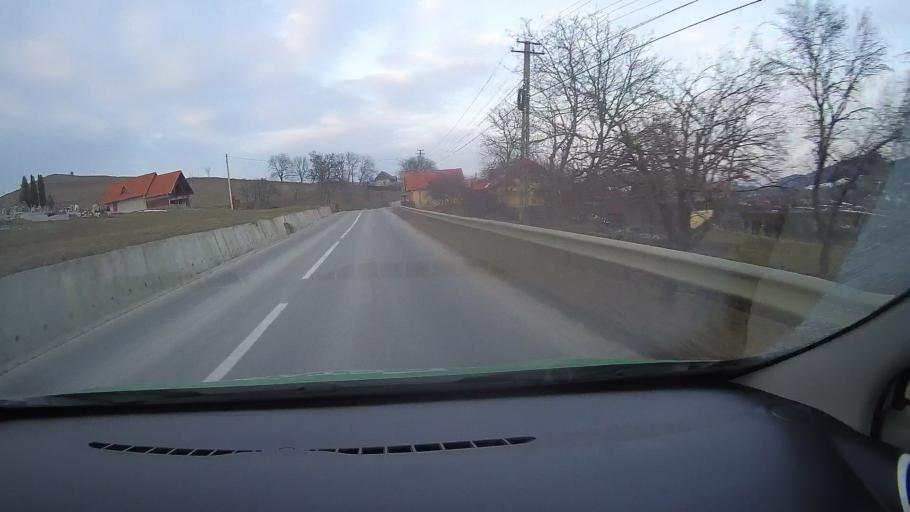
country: RO
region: Harghita
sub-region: Comuna Lupeni
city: Lupeni
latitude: 46.3591
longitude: 25.1696
